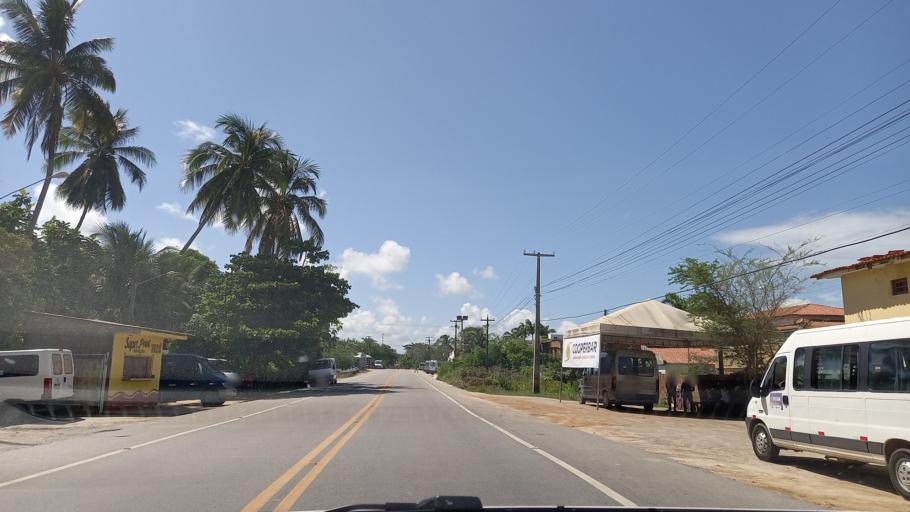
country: BR
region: Pernambuco
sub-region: Sao Jose Da Coroa Grande
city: Sao Jose da Coroa Grande
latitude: -8.9159
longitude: -35.1539
